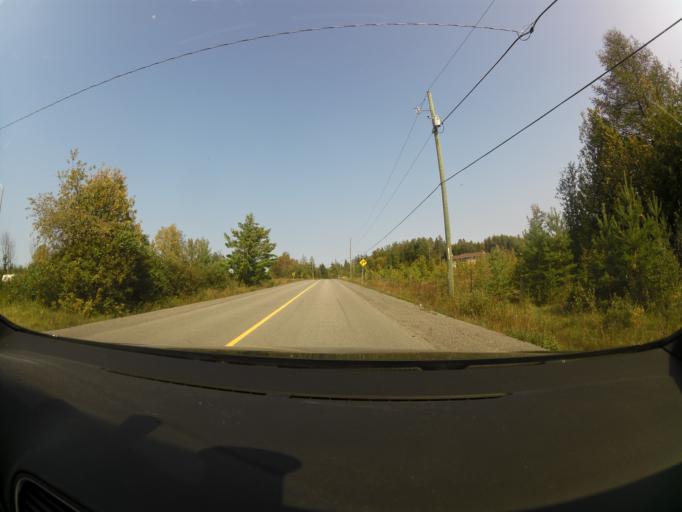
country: CA
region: Ontario
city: Carleton Place
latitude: 45.3303
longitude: -76.1635
